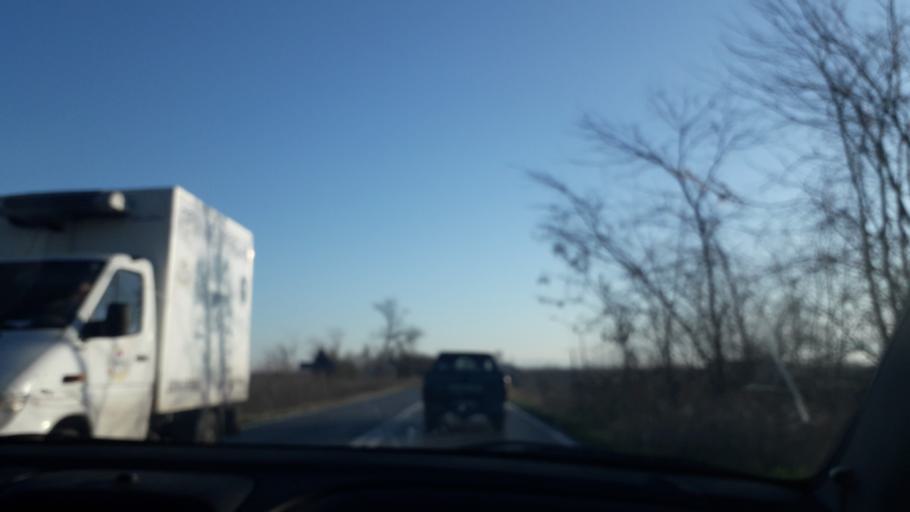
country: GR
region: Central Macedonia
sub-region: Nomos Pellis
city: Giannitsa
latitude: 40.7265
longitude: 22.4078
